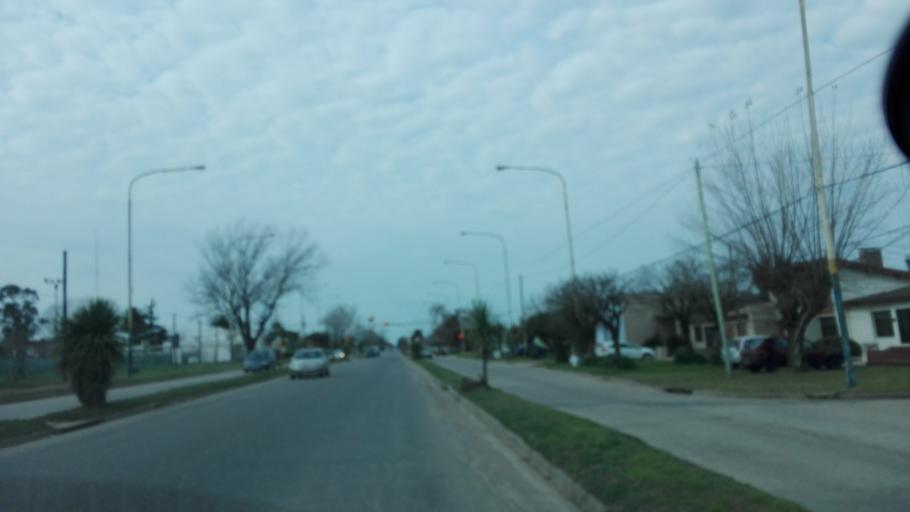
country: AR
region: Buenos Aires
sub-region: Partido de Chascomus
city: Chascomus
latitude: -35.5764
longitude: -58.0025
